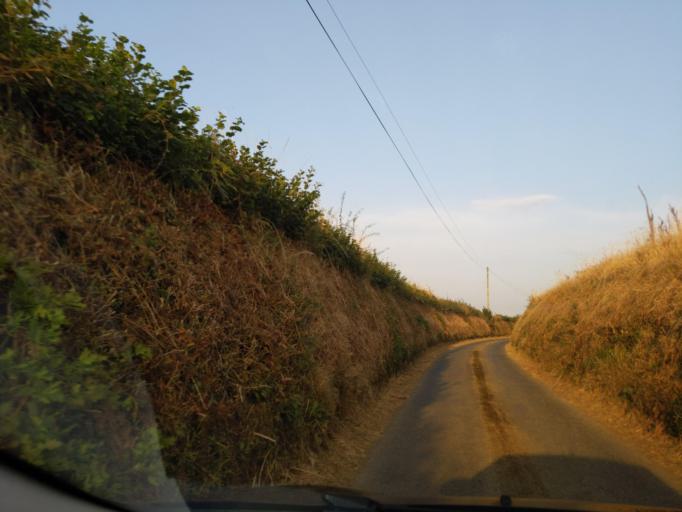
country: GB
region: England
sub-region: Cornwall
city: Fowey
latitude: 50.3676
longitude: -4.5878
